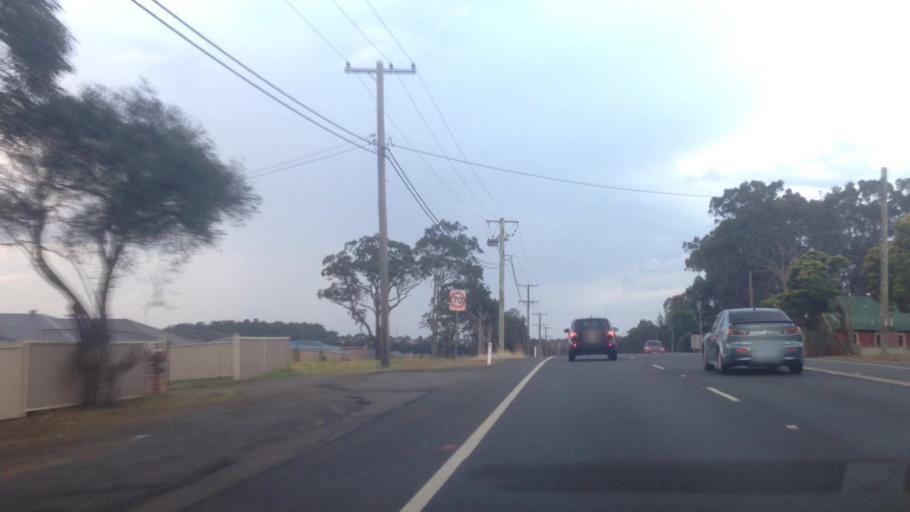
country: AU
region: New South Wales
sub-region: Wyong Shire
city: Kanwal
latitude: -33.2596
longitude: 151.4848
